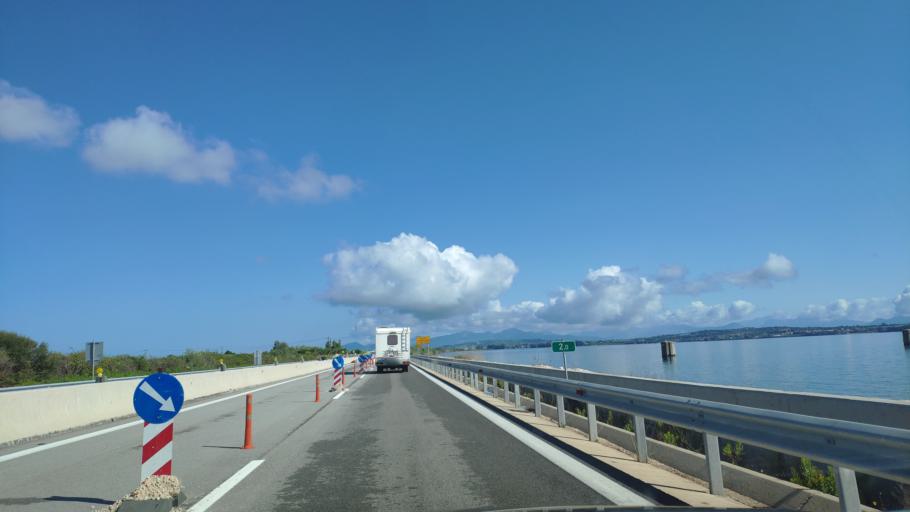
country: GR
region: Epirus
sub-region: Nomos Prevezis
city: Preveza
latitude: 38.9294
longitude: 20.7827
